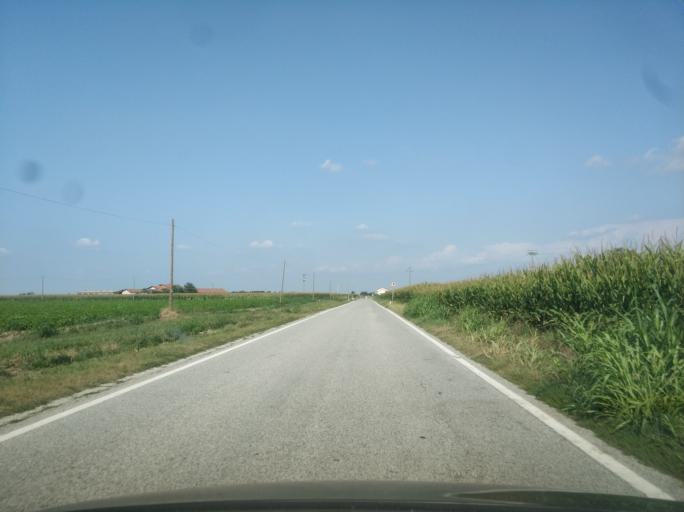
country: IT
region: Piedmont
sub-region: Provincia di Cuneo
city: Genola
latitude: 44.5344
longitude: 7.6540
